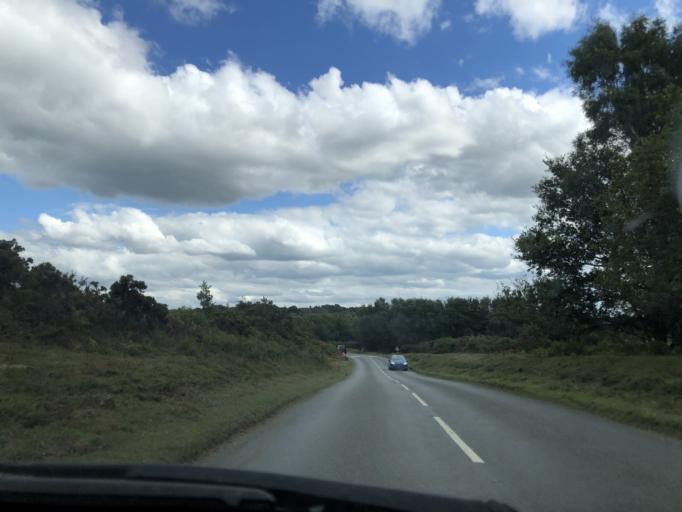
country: GB
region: England
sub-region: East Sussex
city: Forest Row
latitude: 51.0402
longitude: 0.0771
